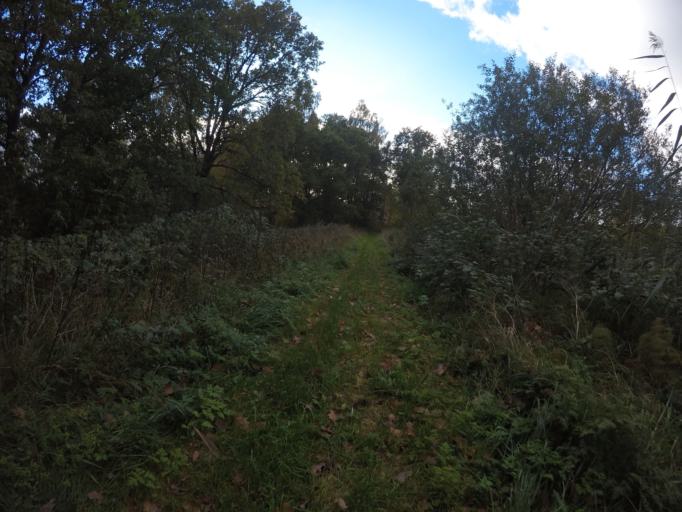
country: SE
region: Vaestmanland
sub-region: Arboga Kommun
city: Tyringe
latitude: 59.2939
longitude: 15.9987
